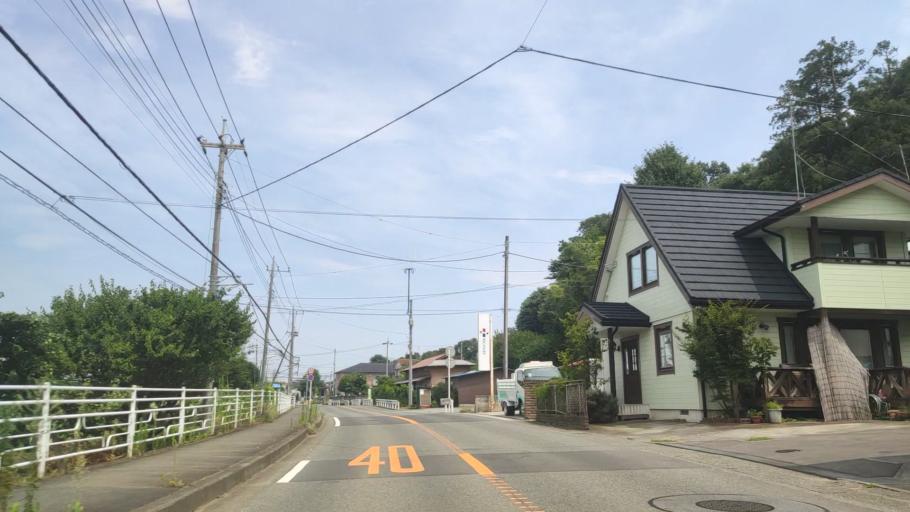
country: JP
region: Kanagawa
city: Atsugi
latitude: 35.4372
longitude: 139.3938
